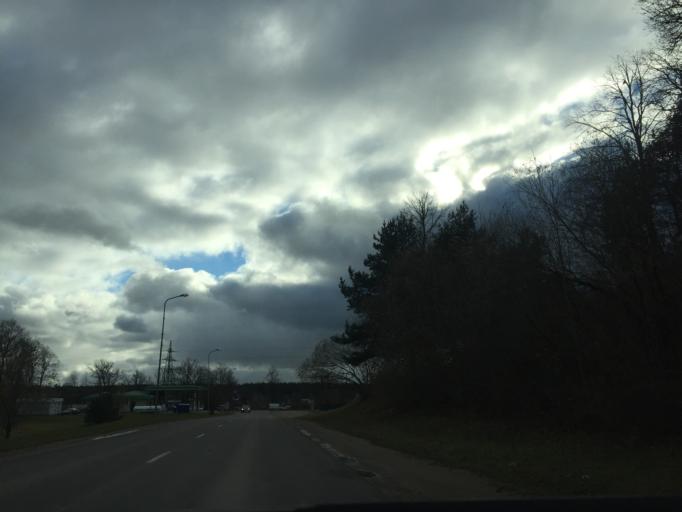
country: LV
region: Tukuma Rajons
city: Tukums
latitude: 56.9641
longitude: 23.1376
